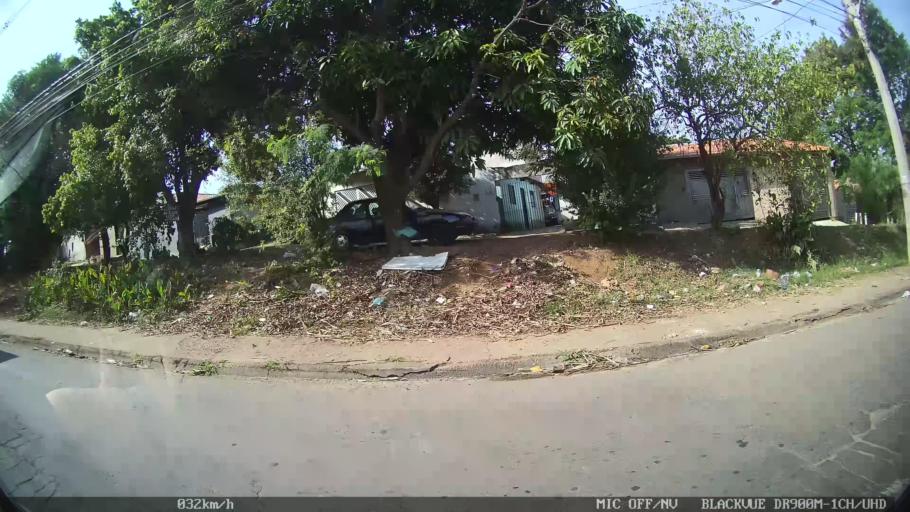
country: BR
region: Sao Paulo
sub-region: Piracicaba
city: Piracicaba
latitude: -22.6955
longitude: -47.6711
